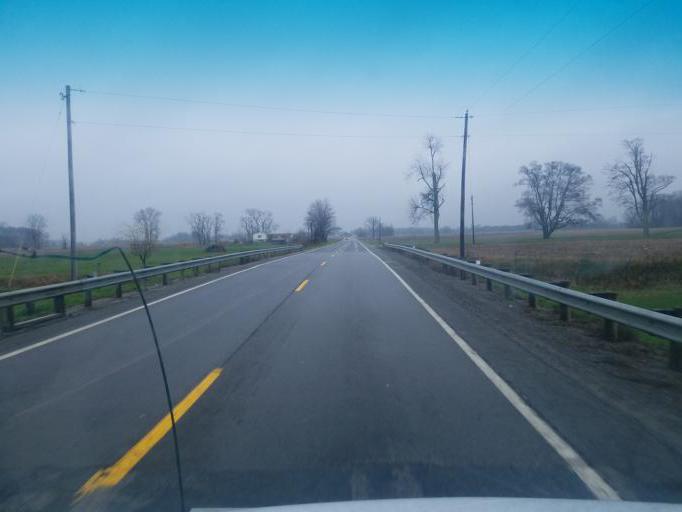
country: US
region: Ohio
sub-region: Wood County
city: Weston
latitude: 41.3722
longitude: -83.7269
